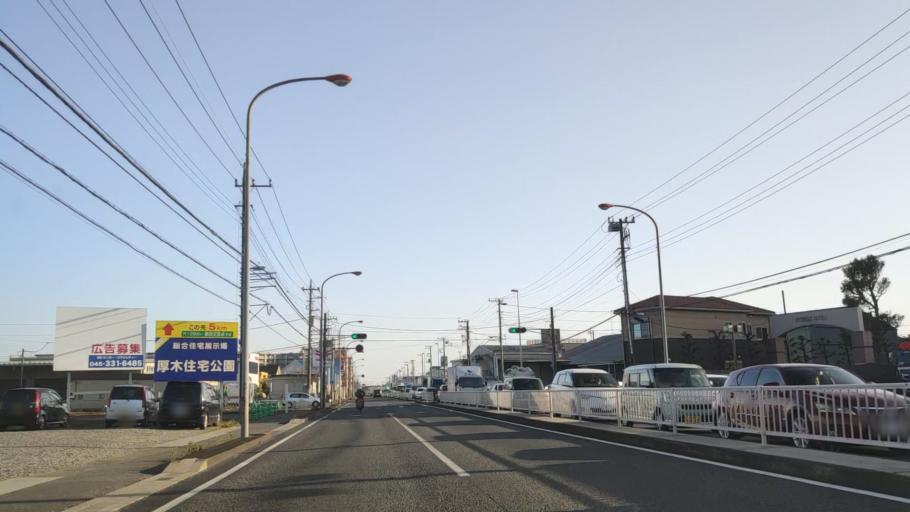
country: JP
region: Kanagawa
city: Zama
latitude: 35.4832
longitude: 139.3656
